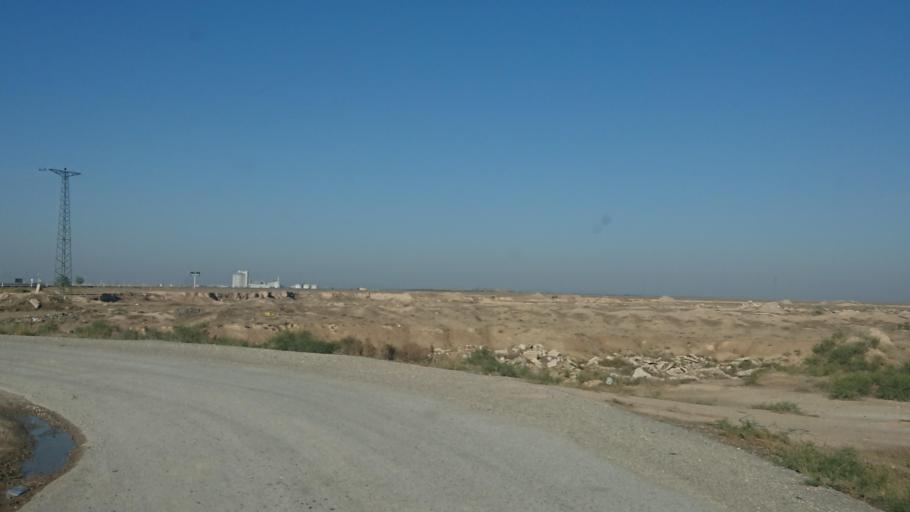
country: TR
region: Aksaray
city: Sultanhani
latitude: 38.2783
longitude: 33.7018
